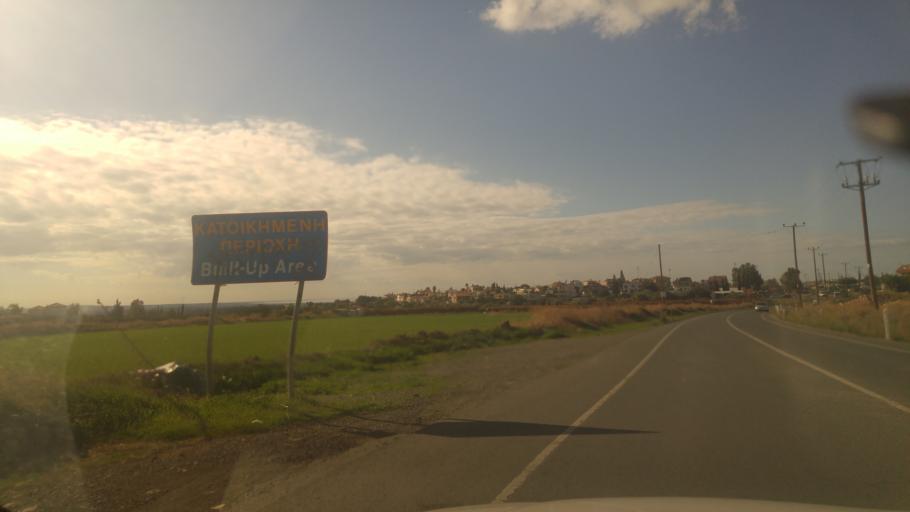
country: CY
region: Larnaka
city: Kolossi
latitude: 34.6780
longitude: 32.9459
